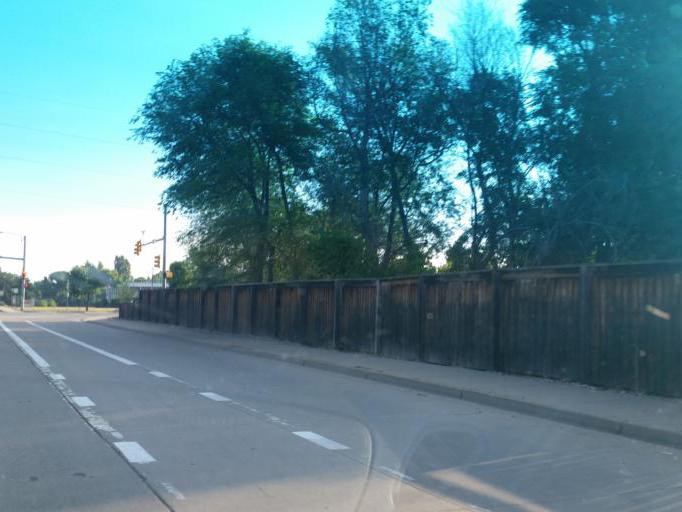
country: US
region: Colorado
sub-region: Larimer County
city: Fort Collins
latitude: 40.5522
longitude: -105.1150
